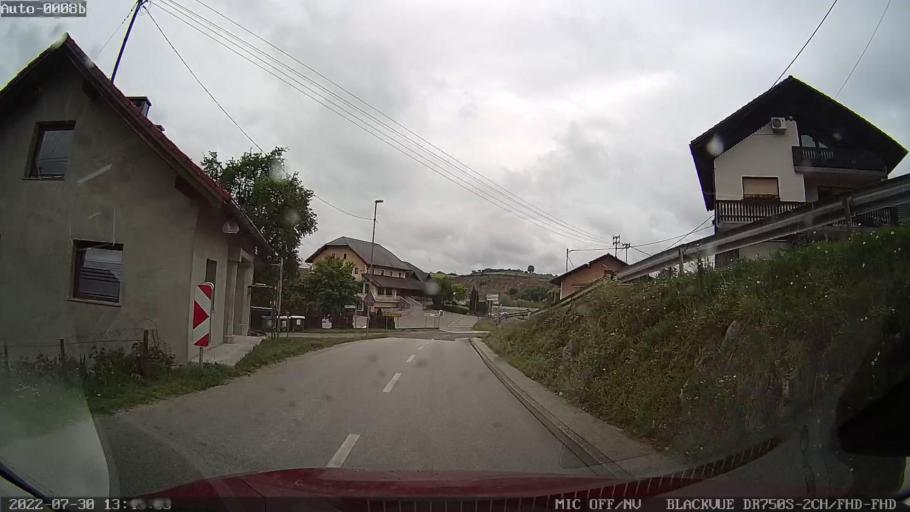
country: SI
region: Ivancna Gorica
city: Sentvid pri Sticni
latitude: 45.9215
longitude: 14.8897
